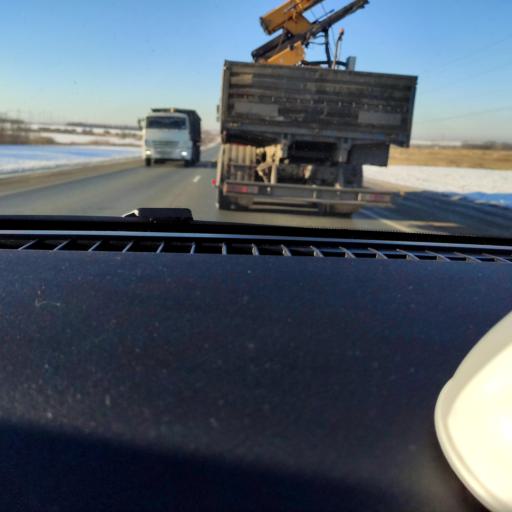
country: RU
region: Samara
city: Smyshlyayevka
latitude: 53.1447
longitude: 50.4605
